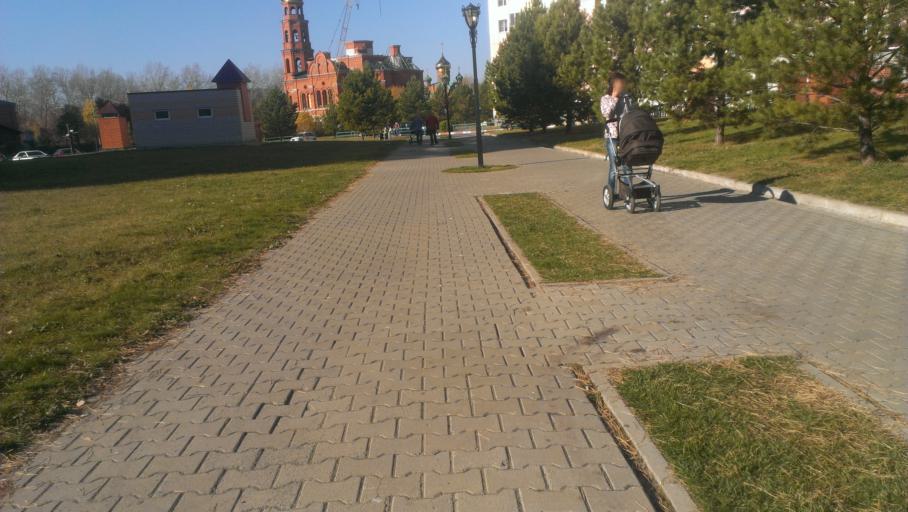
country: RU
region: Altai Krai
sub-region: Gorod Barnaulskiy
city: Barnaul
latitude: 53.3580
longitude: 83.6921
